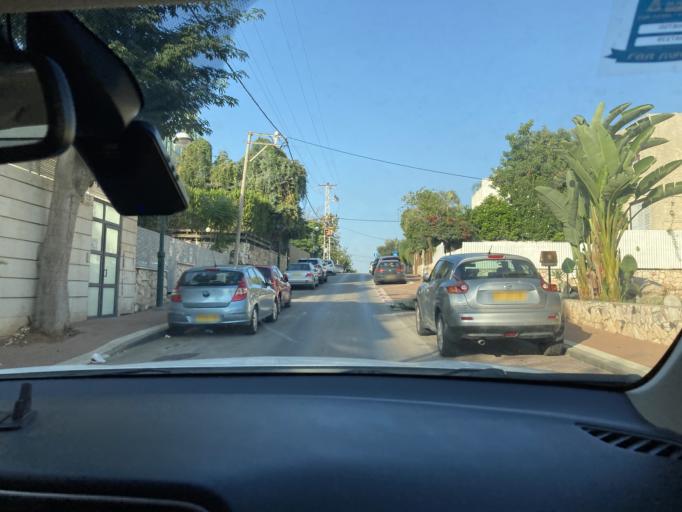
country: IL
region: Tel Aviv
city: Ramat HaSharon
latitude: 32.1482
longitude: 34.8367
